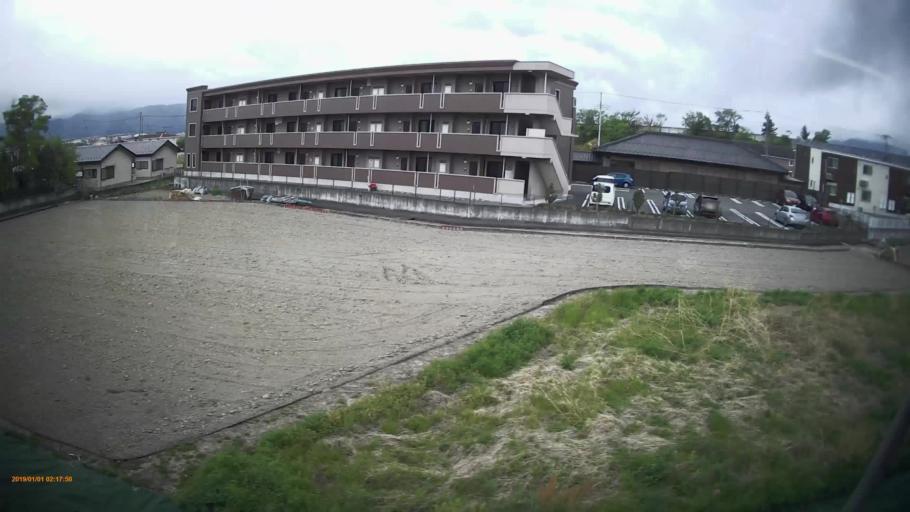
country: JP
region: Yamanashi
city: Ryuo
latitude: 35.6691
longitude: 138.5277
